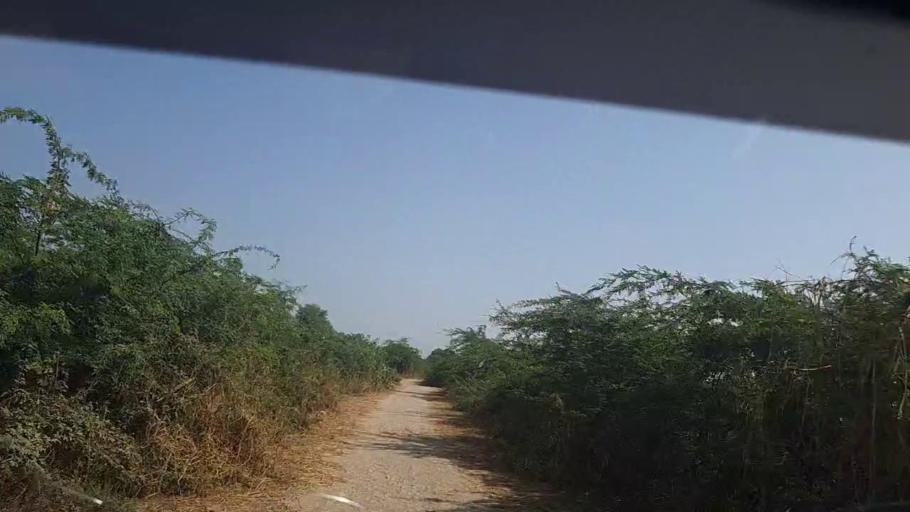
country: PK
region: Sindh
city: Rajo Khanani
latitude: 24.9567
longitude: 68.8953
